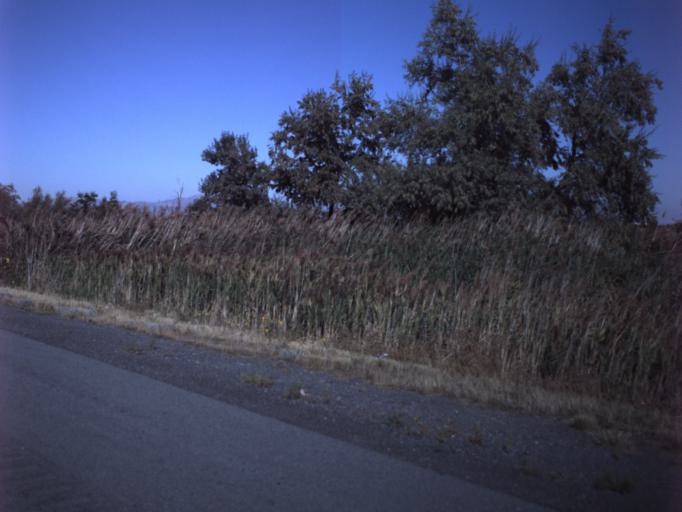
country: US
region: Utah
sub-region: Salt Lake County
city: Magna
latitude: 40.7280
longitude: -112.1779
